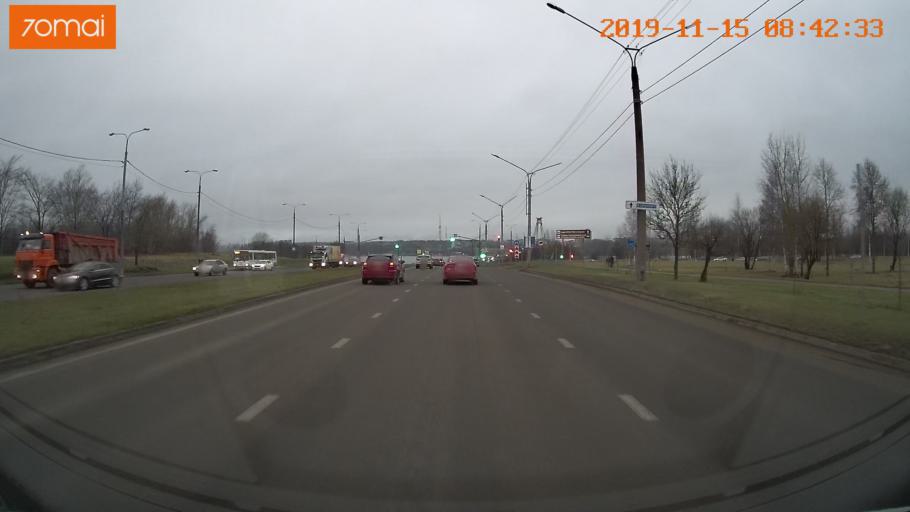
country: RU
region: Vologda
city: Cherepovets
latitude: 59.1037
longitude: 37.9074
